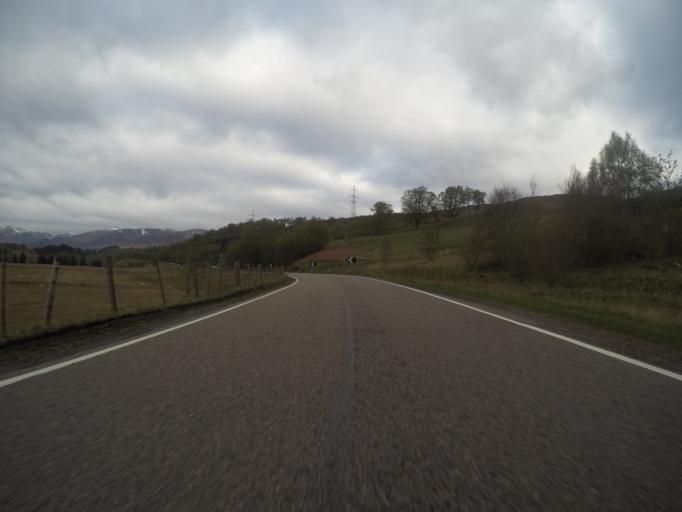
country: GB
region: Scotland
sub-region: Highland
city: Kingussie
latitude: 56.9752
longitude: -4.3874
